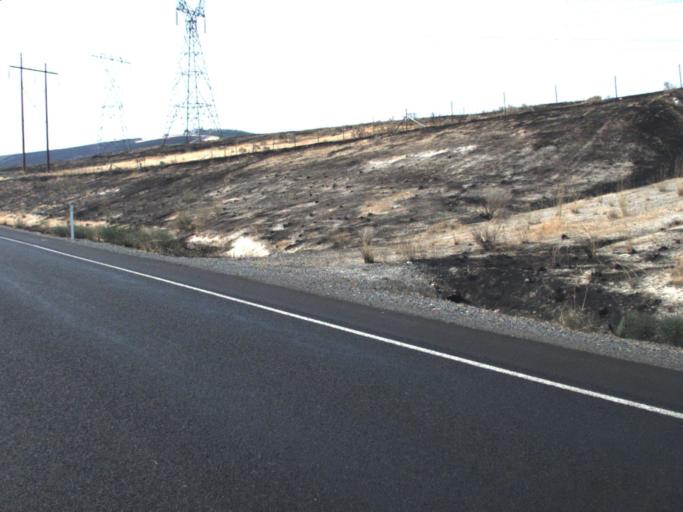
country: US
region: Washington
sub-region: Grant County
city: Desert Aire
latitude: 46.5557
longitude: -119.8151
